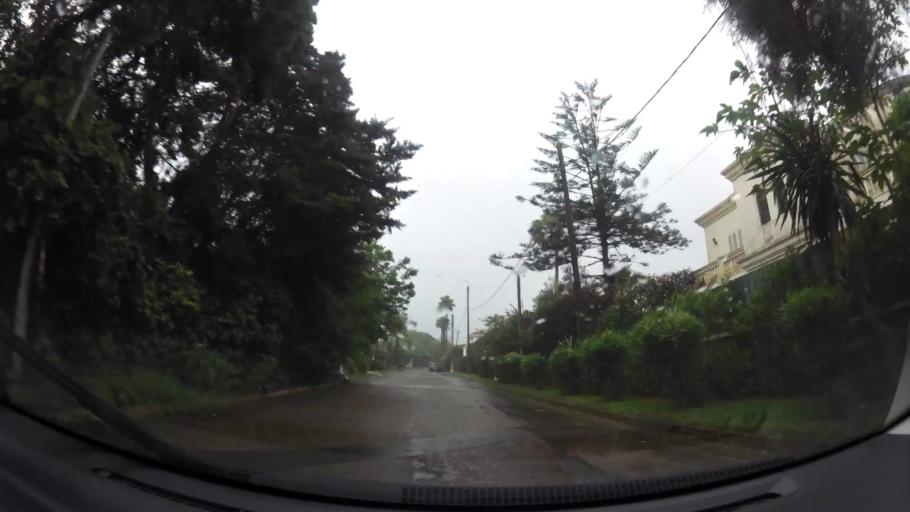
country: MA
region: Grand Casablanca
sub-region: Casablanca
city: Casablanca
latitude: 33.5871
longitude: -7.6771
